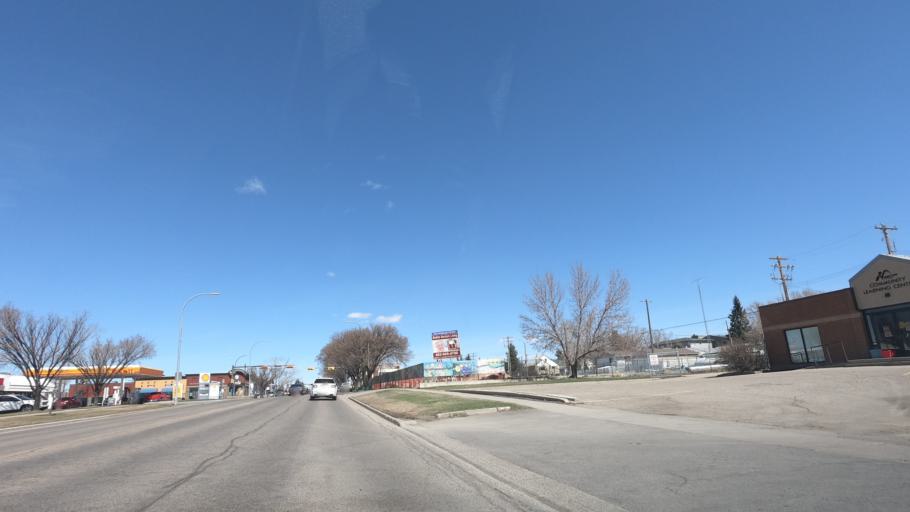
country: CA
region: Alberta
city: Airdrie
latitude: 51.2904
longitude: -114.0134
